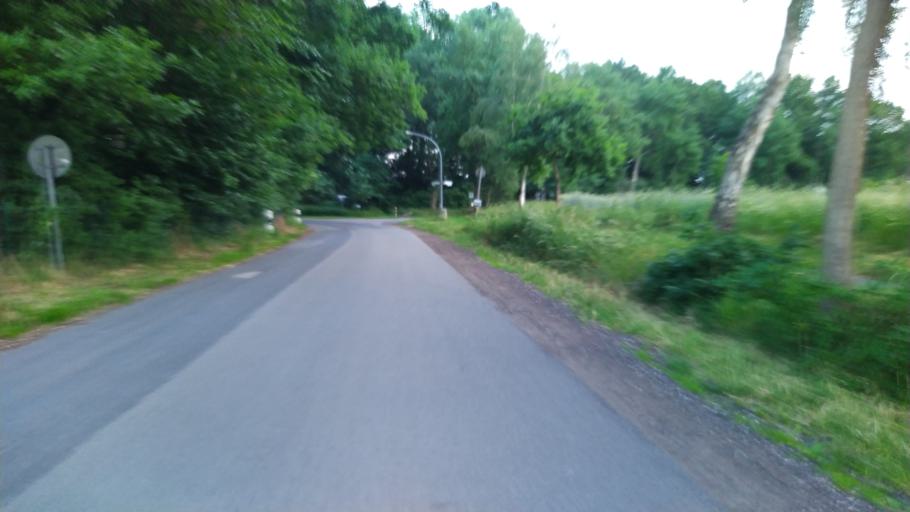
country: DE
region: Lower Saxony
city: Bremervorde
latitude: 53.4843
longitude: 9.1896
